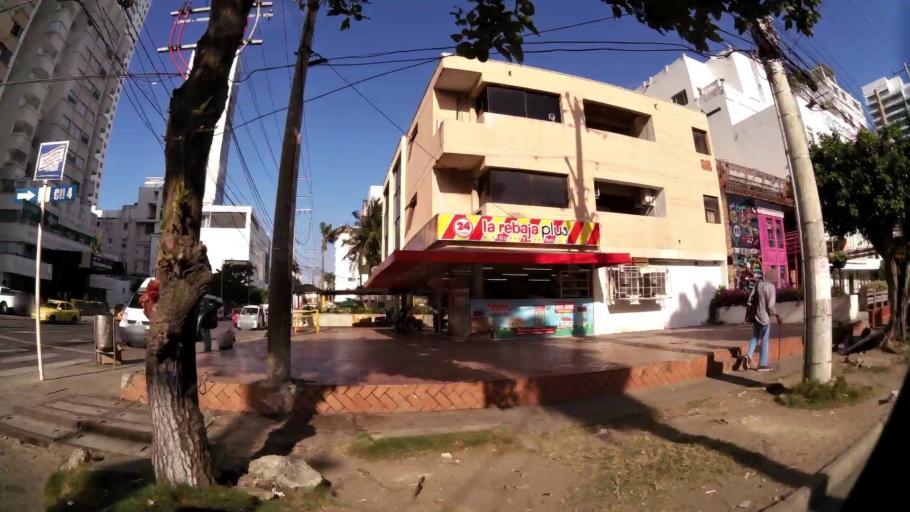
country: CO
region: Bolivar
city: Cartagena
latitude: 10.3986
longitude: -75.5601
